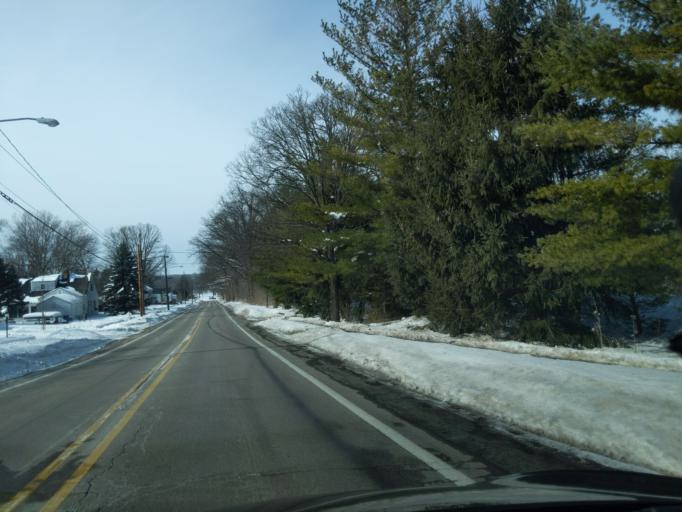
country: US
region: Michigan
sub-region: Kent County
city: Comstock Park
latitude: 43.0135
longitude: -85.6586
